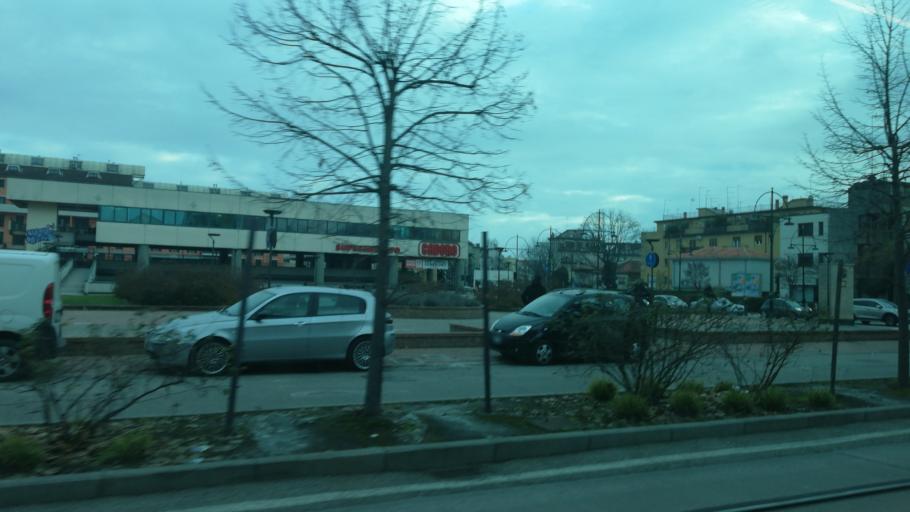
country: IT
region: Veneto
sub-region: Provincia di Venezia
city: Mestre
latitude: 45.4976
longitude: 12.2500
